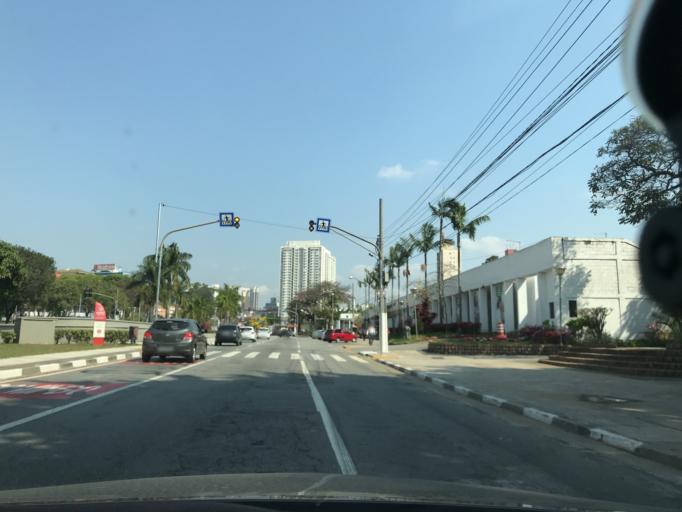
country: BR
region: Sao Paulo
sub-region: Osasco
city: Osasco
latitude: -23.5406
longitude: -46.7728
